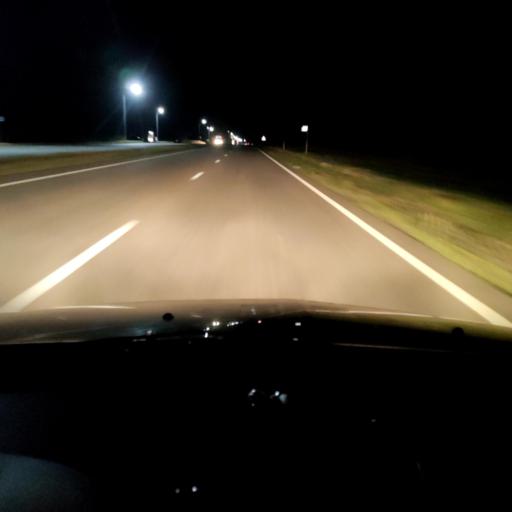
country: RU
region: Belgorod
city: Staryy Oskol
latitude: 51.4192
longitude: 37.8904
